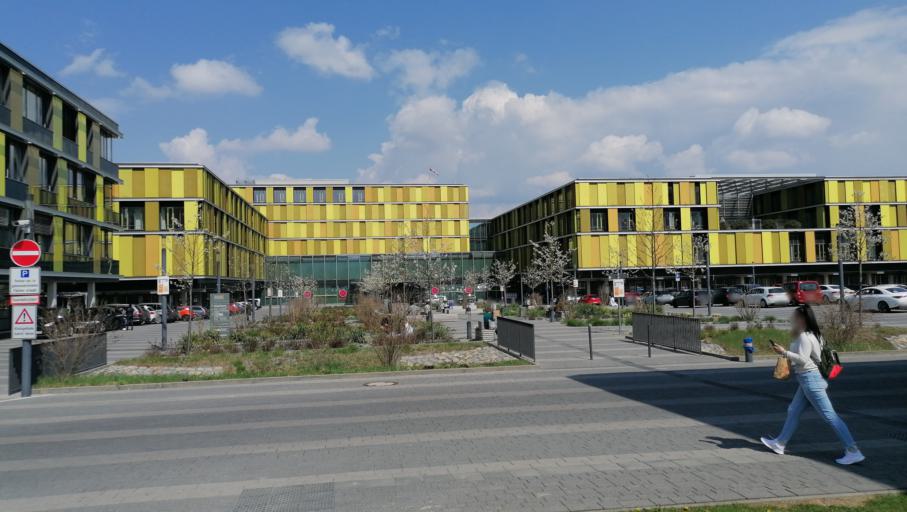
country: DE
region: Baden-Wuerttemberg
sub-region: Regierungsbezirk Stuttgart
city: Winnenden
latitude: 48.8691
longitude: 9.3922
